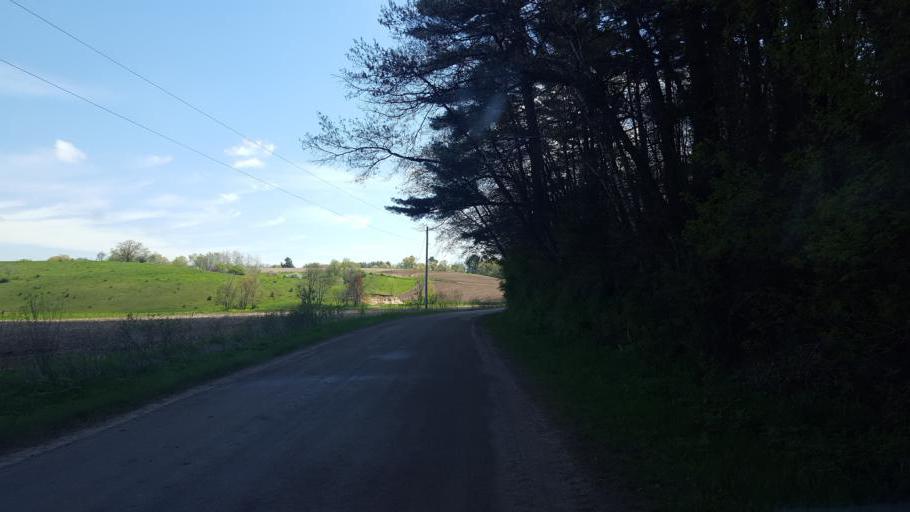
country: US
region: Wisconsin
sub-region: Juneau County
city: Elroy
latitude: 43.7248
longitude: -90.2870
